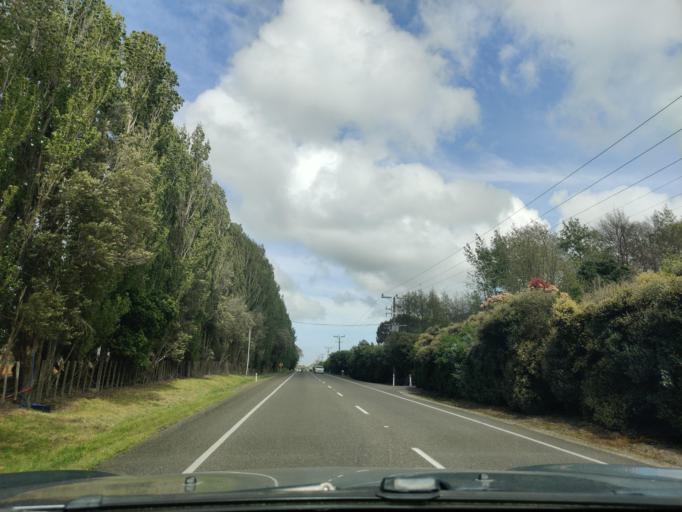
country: NZ
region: Manawatu-Wanganui
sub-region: Wanganui District
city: Wanganui
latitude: -39.8692
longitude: 174.9864
